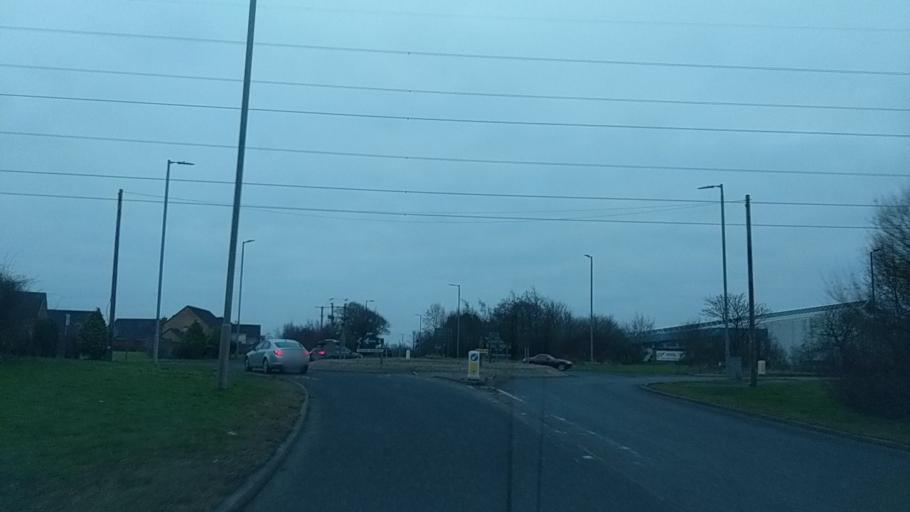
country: GB
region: Scotland
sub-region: South Lanarkshire
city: East Kilbride
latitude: 55.7431
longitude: -4.1580
